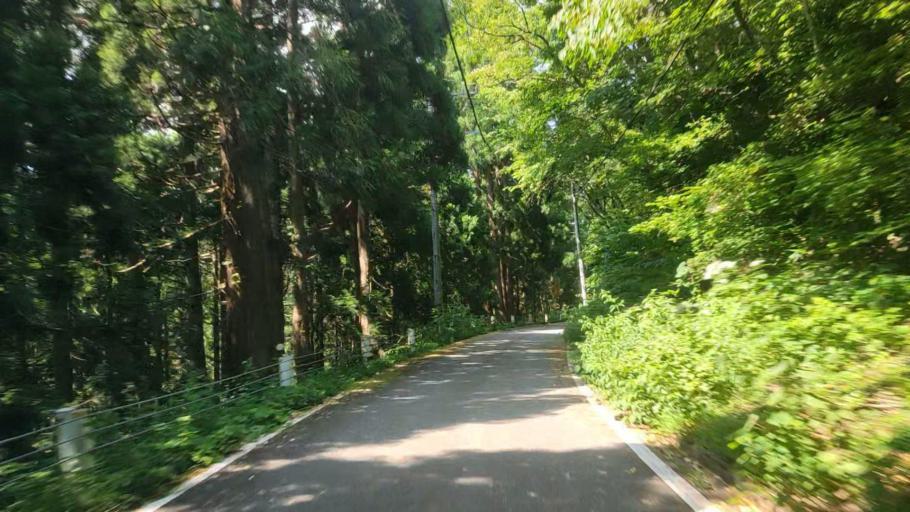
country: JP
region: Fukui
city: Katsuyama
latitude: 36.2392
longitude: 136.5302
